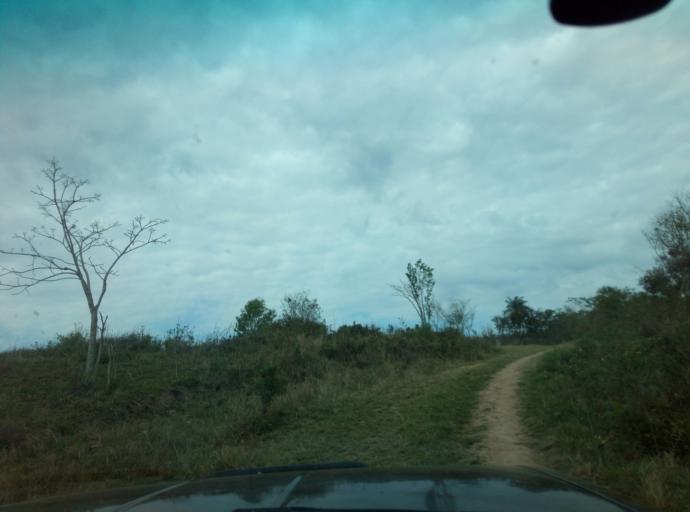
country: PY
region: Caaguazu
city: Doctor Cecilio Baez
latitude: -25.1998
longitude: -56.1273
